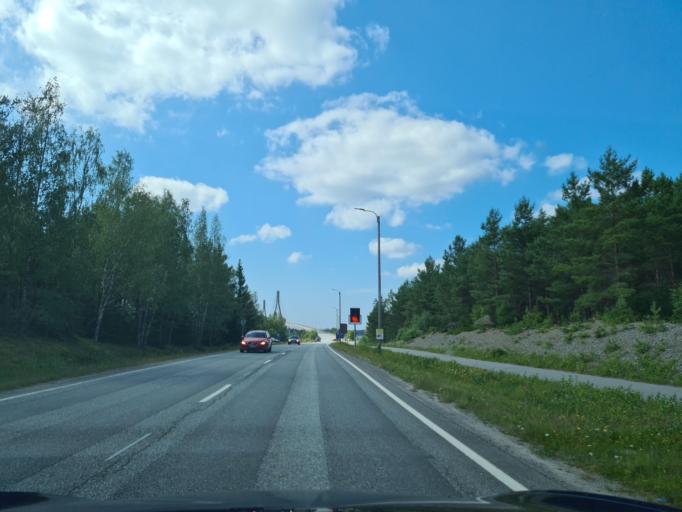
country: FI
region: Ostrobothnia
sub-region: Vaasa
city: Replot
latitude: 63.2058
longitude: 21.4937
